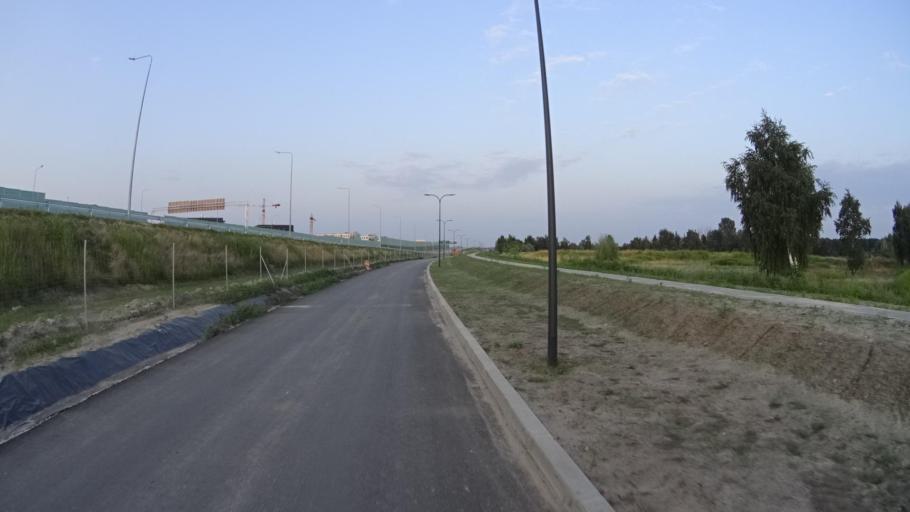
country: PL
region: Masovian Voivodeship
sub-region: Warszawa
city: Wilanow
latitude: 52.1527
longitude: 21.0743
